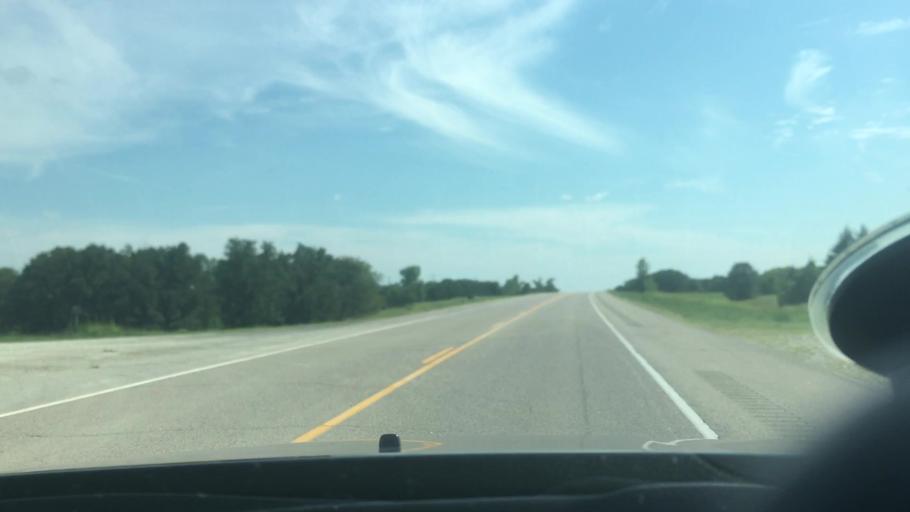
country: US
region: Oklahoma
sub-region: Seminole County
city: Seminole
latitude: 35.1416
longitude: -96.6762
